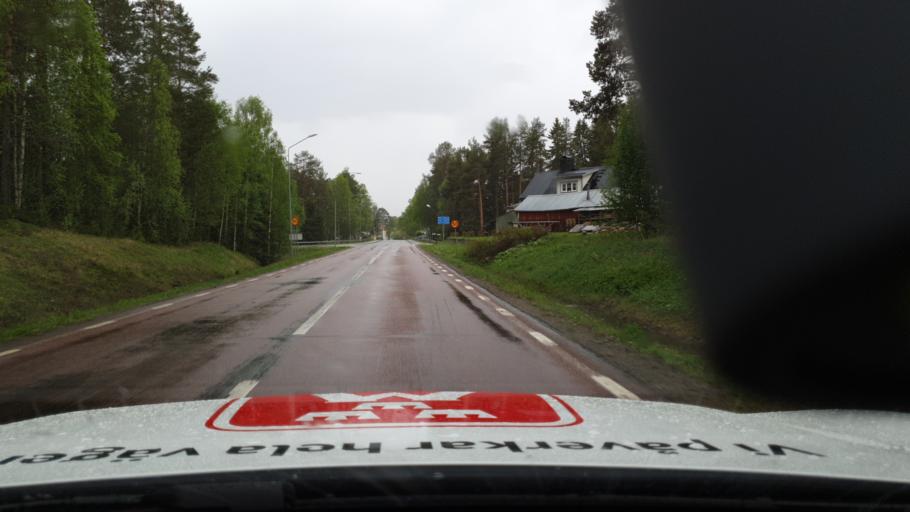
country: SE
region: Vaesterbotten
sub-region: Dorotea Kommun
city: Dorotea
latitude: 64.1214
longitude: 16.2086
